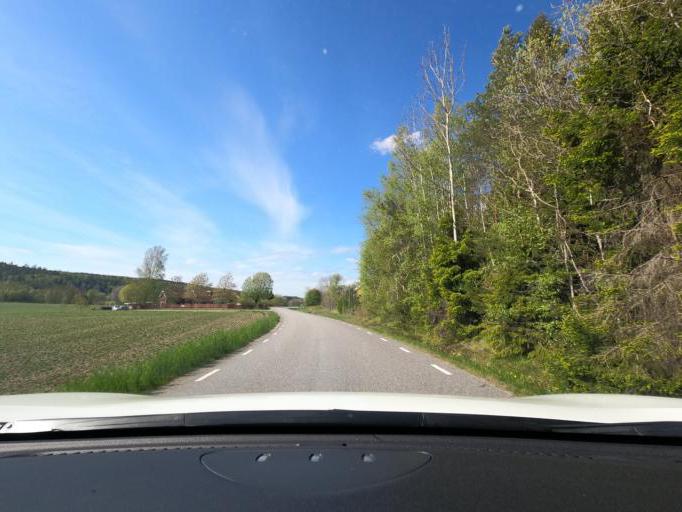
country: SE
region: Vaestra Goetaland
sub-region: Harryda Kommun
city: Ravlanda
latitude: 57.6166
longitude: 12.4959
